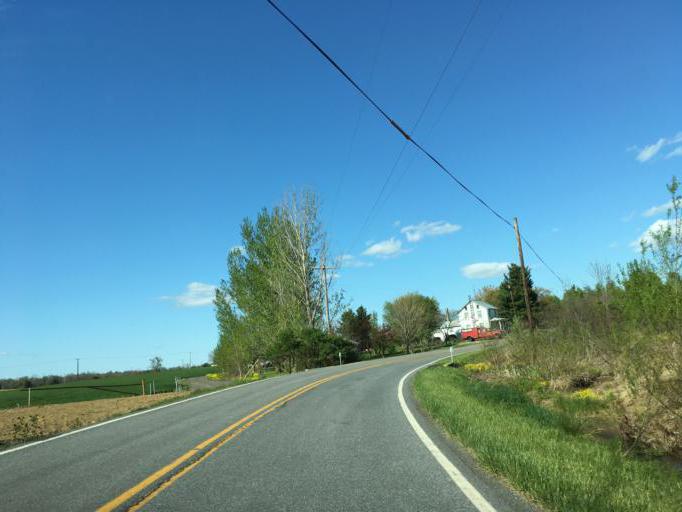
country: US
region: Maryland
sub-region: Frederick County
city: Emmitsburg
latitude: 39.6623
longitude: -77.3526
